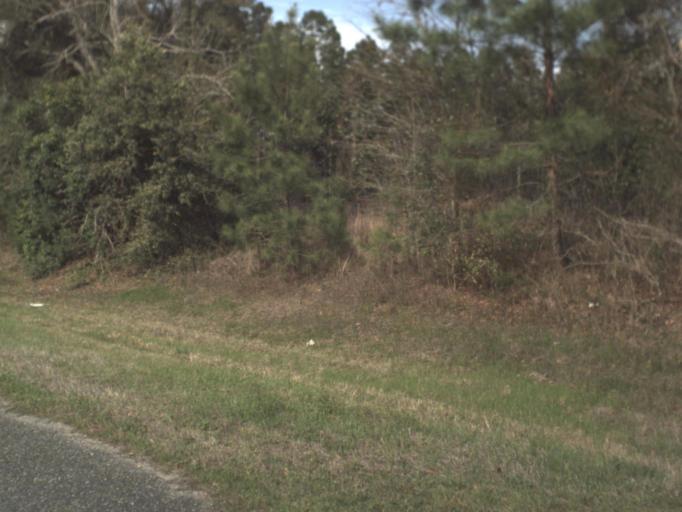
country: US
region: Florida
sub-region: Jefferson County
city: Monticello
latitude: 30.4181
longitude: -83.9109
